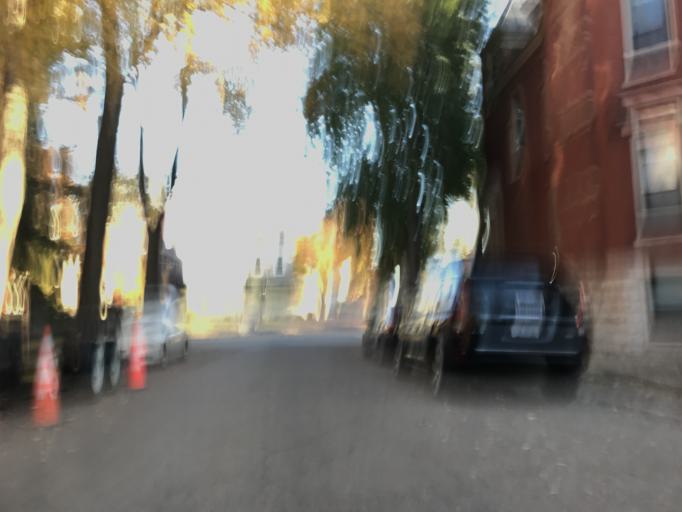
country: US
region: Kentucky
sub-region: Jefferson County
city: Louisville
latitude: 38.2436
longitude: -85.7299
